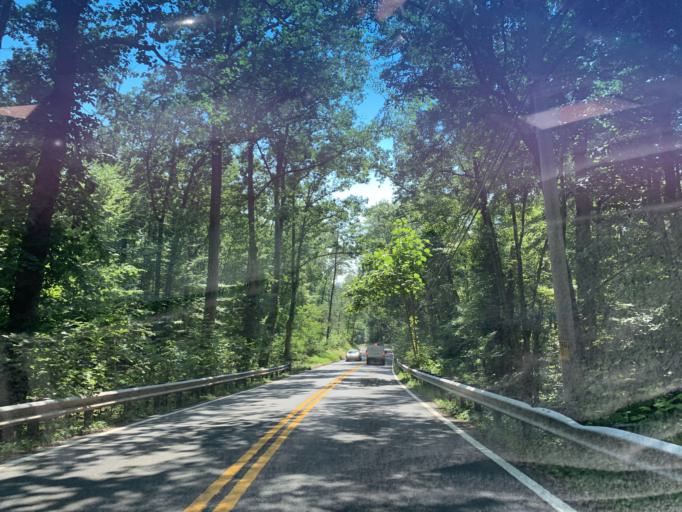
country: US
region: Maryland
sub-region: Montgomery County
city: Clarksburg
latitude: 39.2296
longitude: -77.3675
